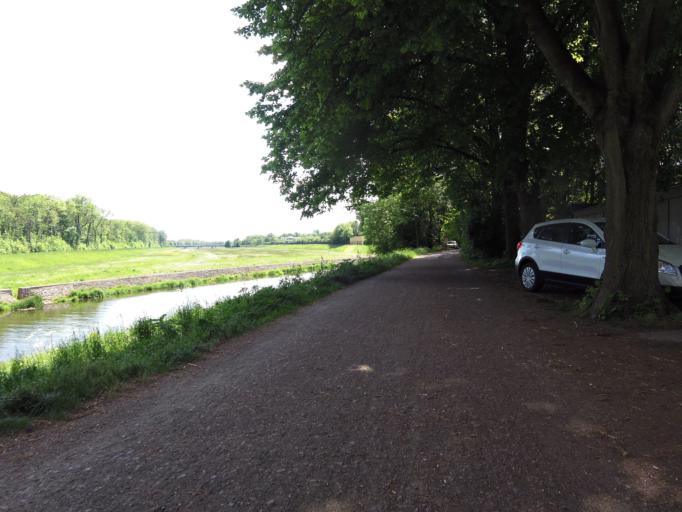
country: DE
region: Saxony
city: Markkleeberg
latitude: 51.3070
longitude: 12.3437
